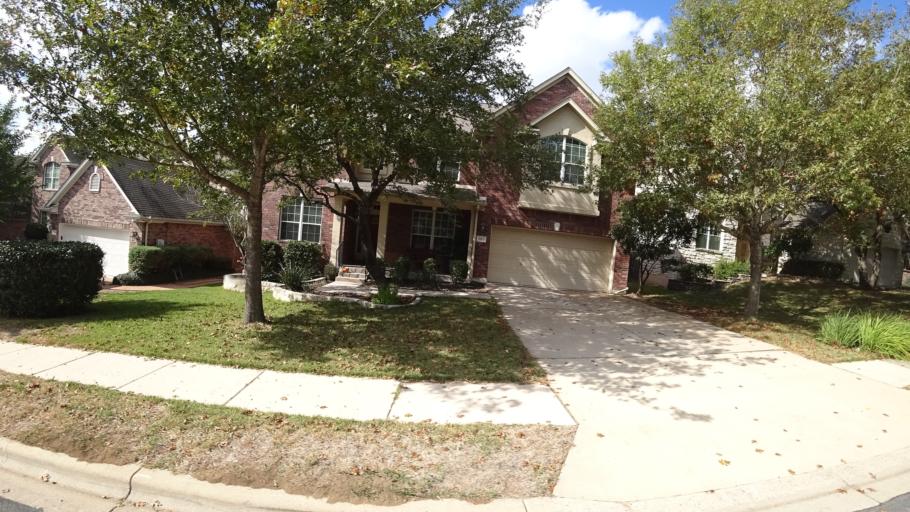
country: US
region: Texas
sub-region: Travis County
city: Barton Creek
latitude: 30.2544
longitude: -97.8845
